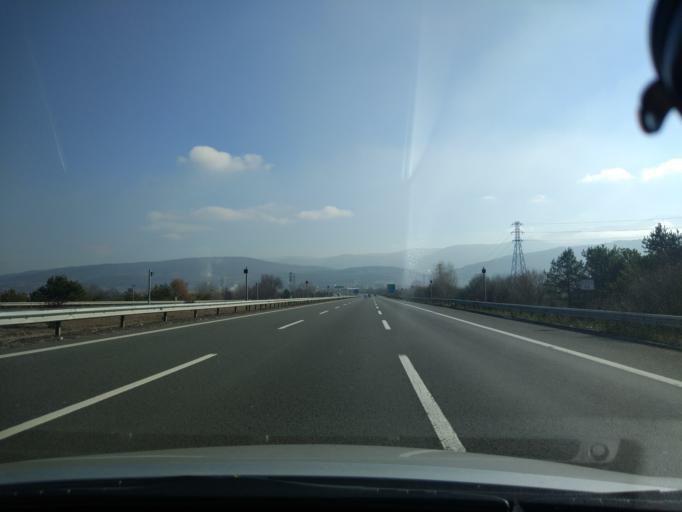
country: TR
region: Bolu
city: Bolu
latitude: 40.7658
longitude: 31.7524
